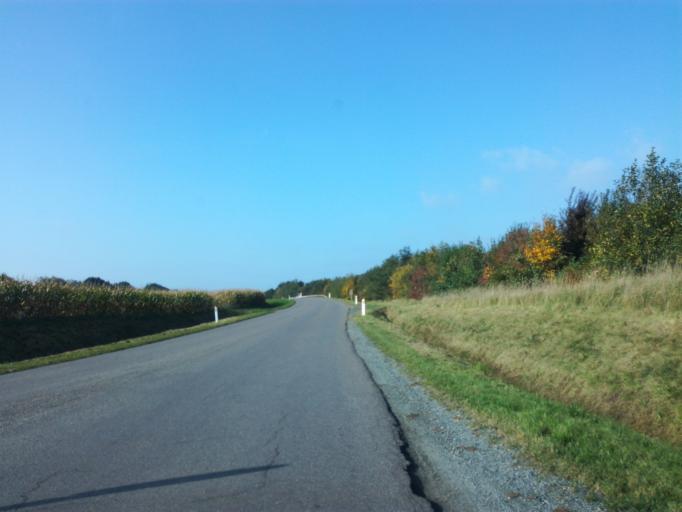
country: DK
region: South Denmark
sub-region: Fredericia Kommune
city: Fredericia
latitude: 55.6257
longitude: 9.7342
